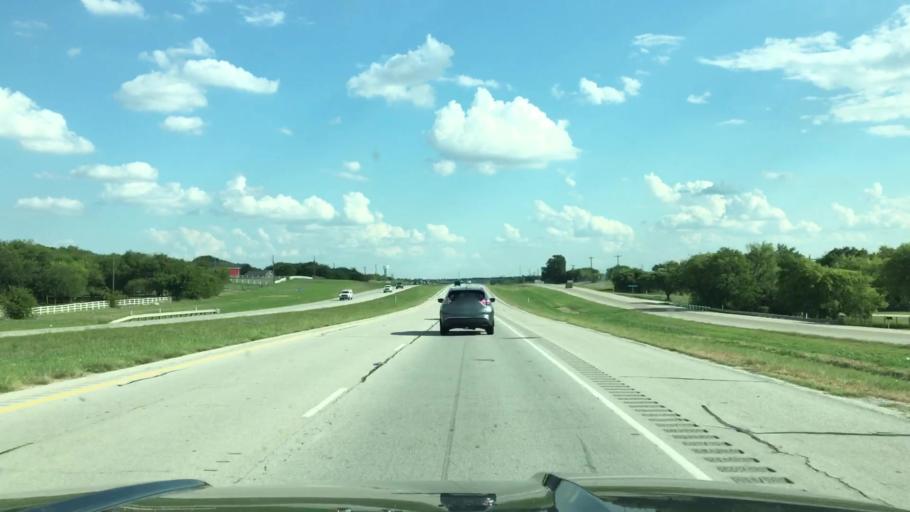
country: US
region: Texas
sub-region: Tarrant County
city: Pecan Acres
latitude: 32.9896
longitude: -97.4299
